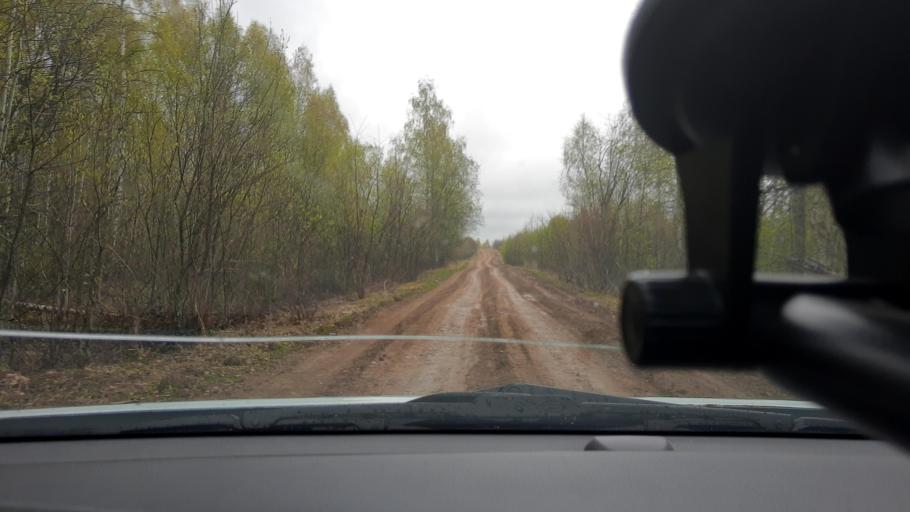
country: RU
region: Bashkortostan
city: Pavlovka
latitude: 55.4341
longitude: 56.3565
